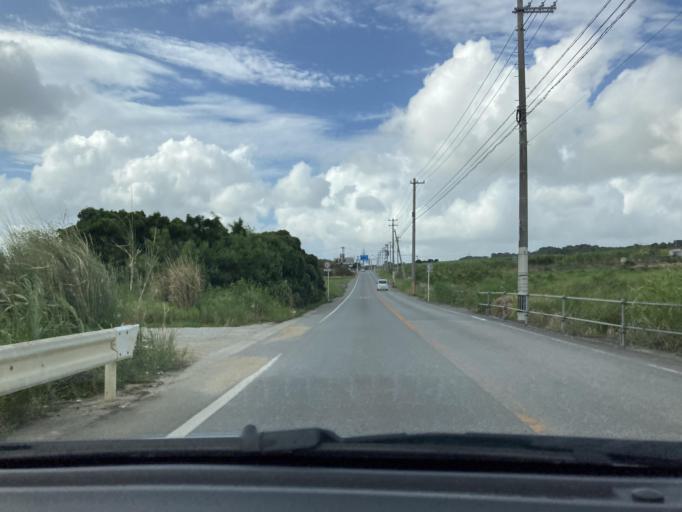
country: JP
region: Okinawa
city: Itoman
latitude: 26.1000
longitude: 127.6979
